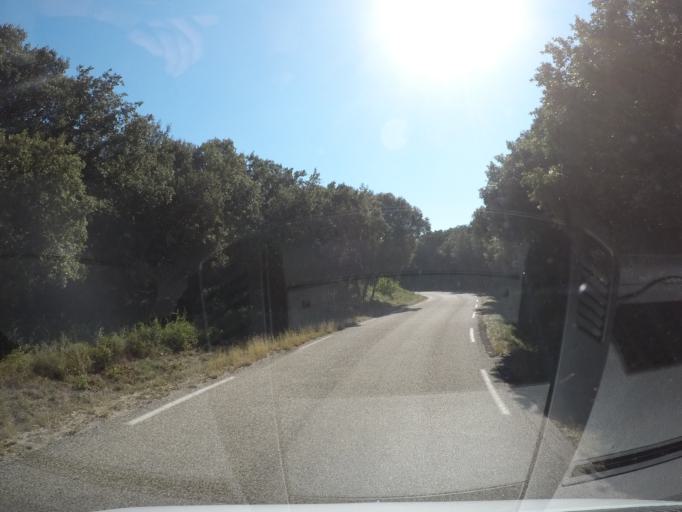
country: FR
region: Languedoc-Roussillon
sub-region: Departement du Gard
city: Castillon-du-Gard
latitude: 44.0110
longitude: 4.6001
